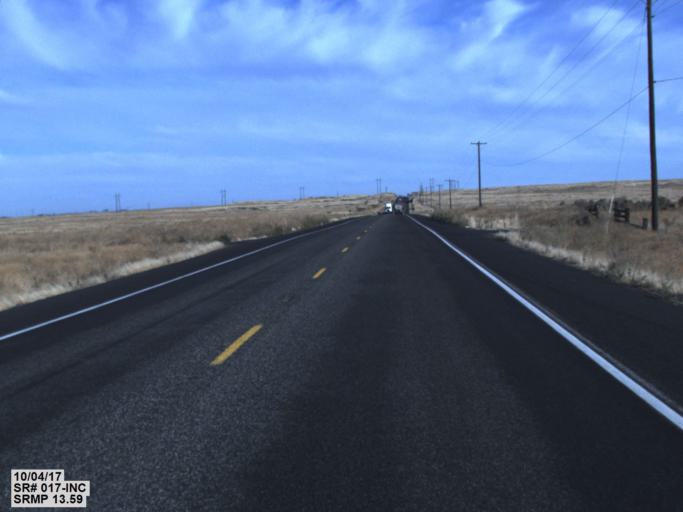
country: US
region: Washington
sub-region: Franklin County
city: Connell
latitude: 46.6491
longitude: -119.0064
